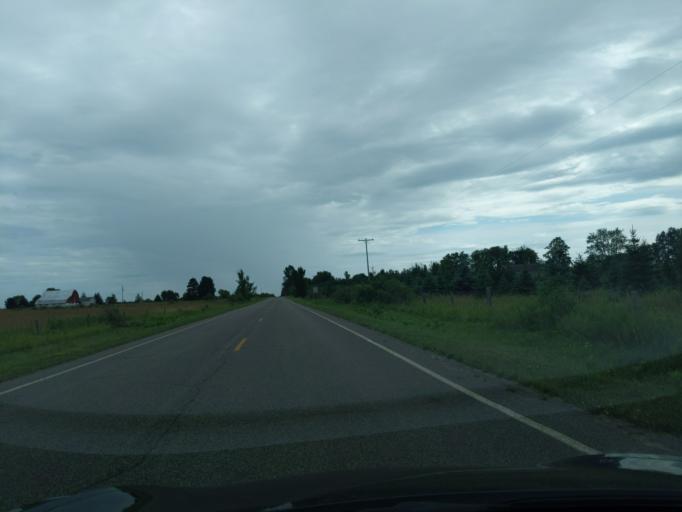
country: US
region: Michigan
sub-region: Clare County
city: Harrison
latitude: 44.0238
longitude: -84.9493
